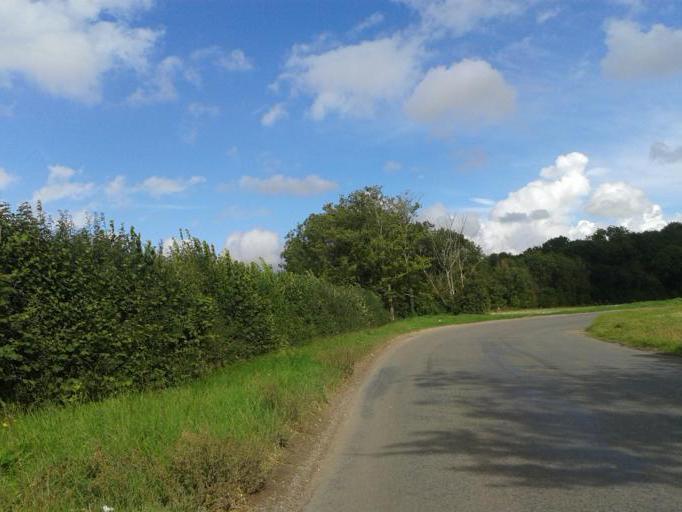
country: GB
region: England
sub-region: Hertfordshire
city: Much Hadham
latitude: 51.9467
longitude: 0.0983
